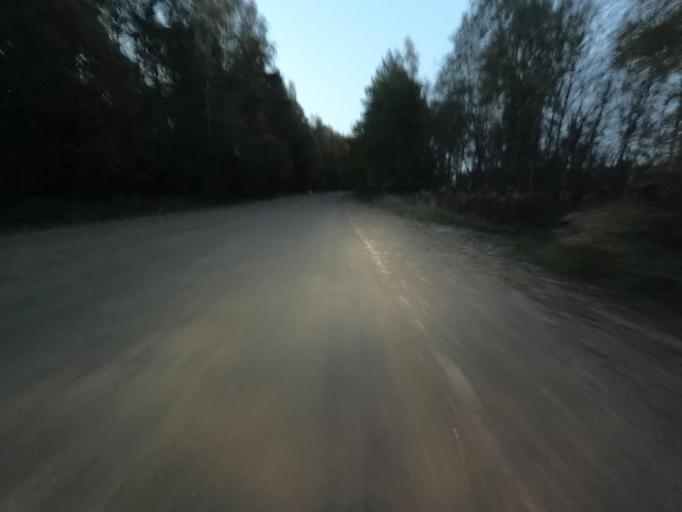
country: RU
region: Leningrad
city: Lyuban'
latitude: 59.1902
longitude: 31.2511
